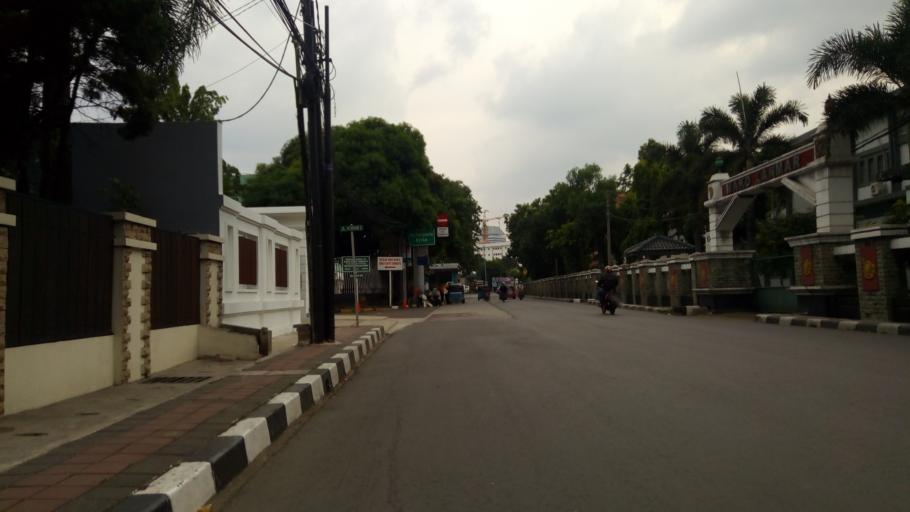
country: ID
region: Jakarta Raya
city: Jakarta
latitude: -6.1749
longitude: 106.8375
